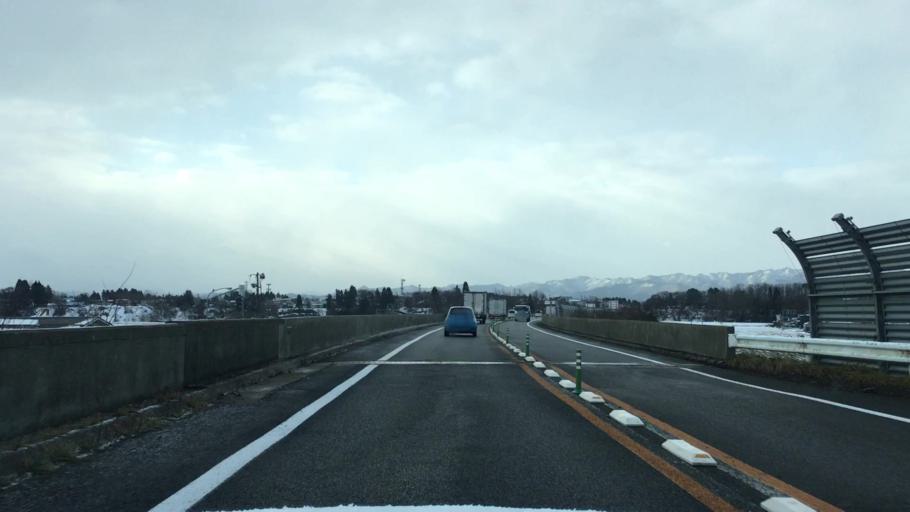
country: JP
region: Akita
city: Odate
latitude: 40.2830
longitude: 140.5402
